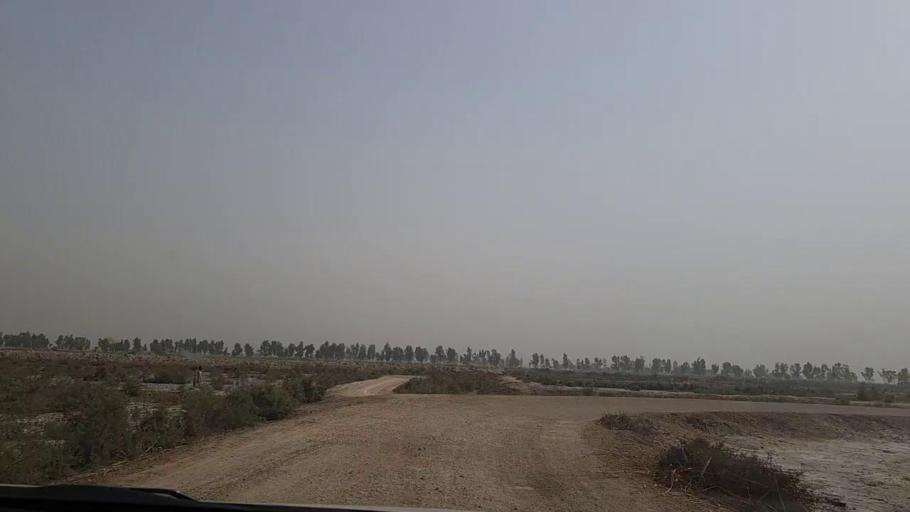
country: PK
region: Sindh
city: Pithoro
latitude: 25.4694
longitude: 69.2297
